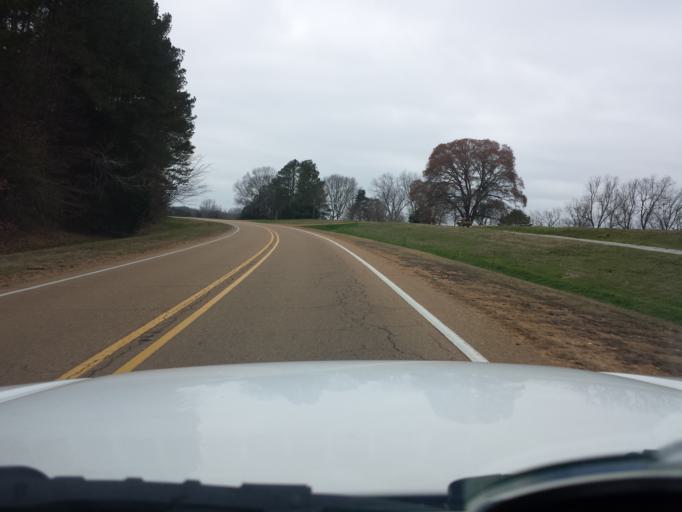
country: US
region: Mississippi
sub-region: Madison County
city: Canton
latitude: 32.7330
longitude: -90.1032
